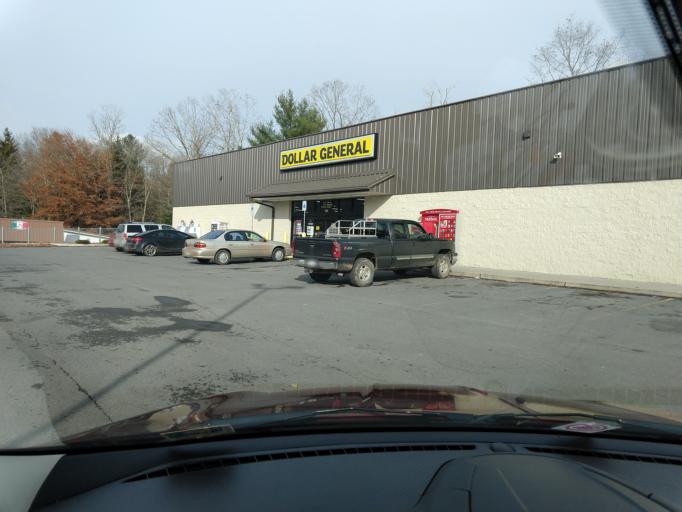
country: US
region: West Virginia
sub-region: Greenbrier County
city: Rainelle
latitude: 37.9644
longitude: -80.6956
